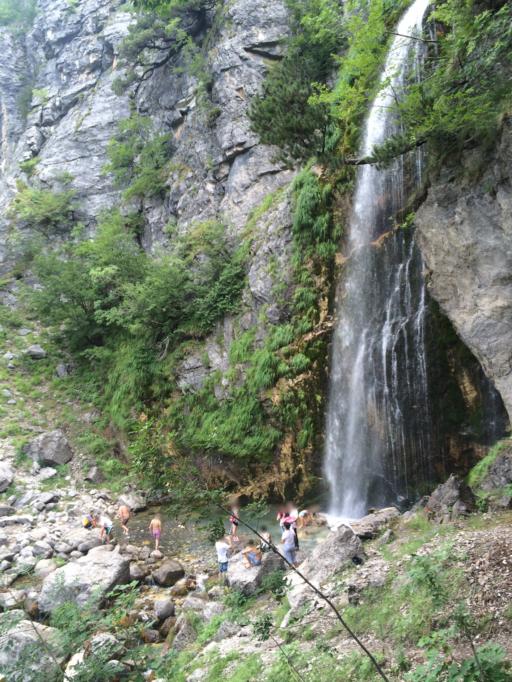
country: AL
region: Shkoder
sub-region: Rrethi i Shkodres
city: Nicaj-Shale
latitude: 42.3773
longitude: 19.7948
